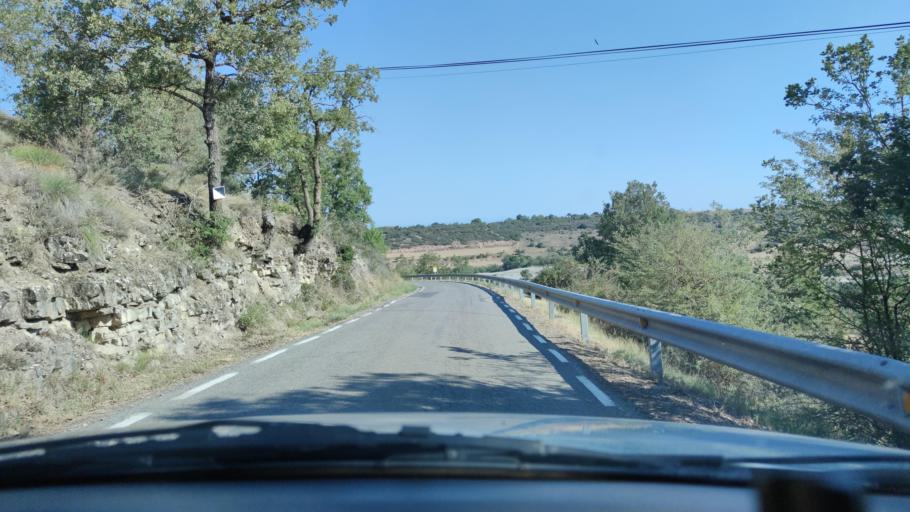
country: ES
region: Catalonia
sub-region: Provincia de Lleida
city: Ivorra
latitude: 41.7322
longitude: 1.3613
